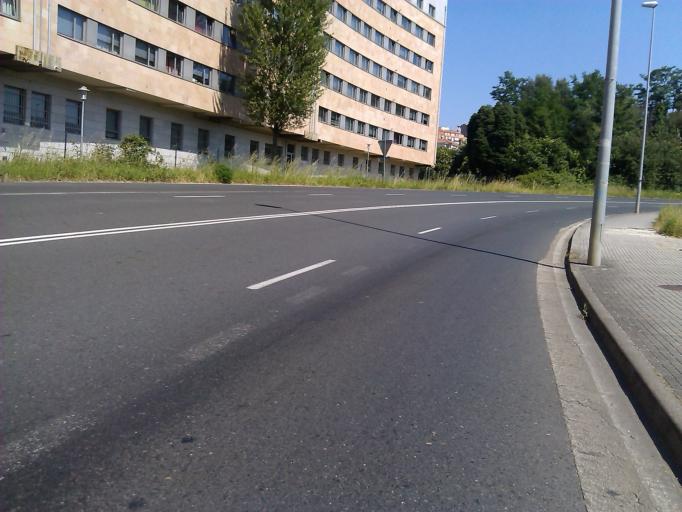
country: ES
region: Galicia
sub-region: Provincia da Coruna
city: Santiago de Compostela
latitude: 42.8684
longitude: -8.5443
